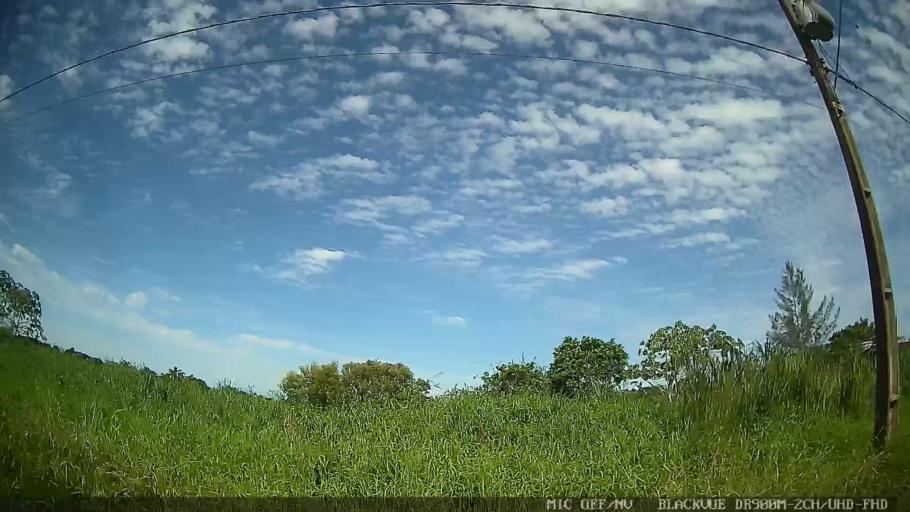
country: BR
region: Sao Paulo
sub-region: Iguape
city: Iguape
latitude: -24.7671
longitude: -47.5919
